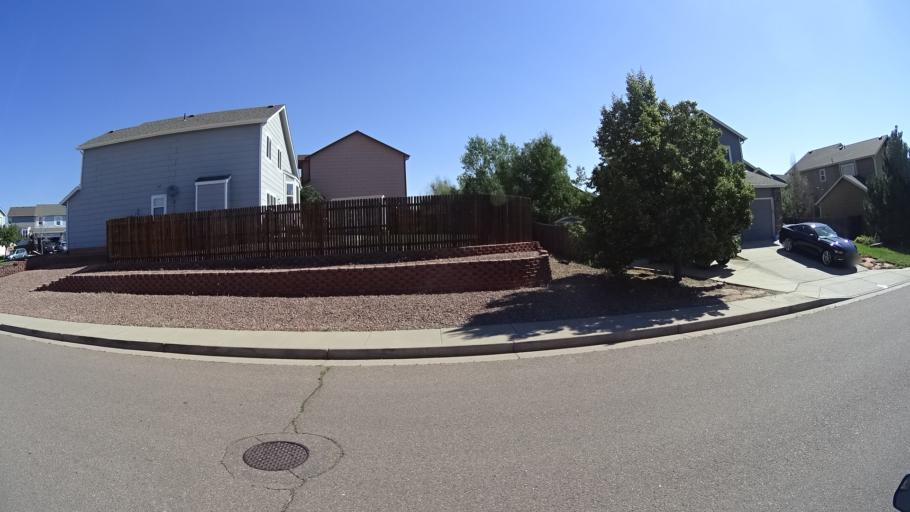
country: US
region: Colorado
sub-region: El Paso County
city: Black Forest
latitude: 38.9452
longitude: -104.7363
